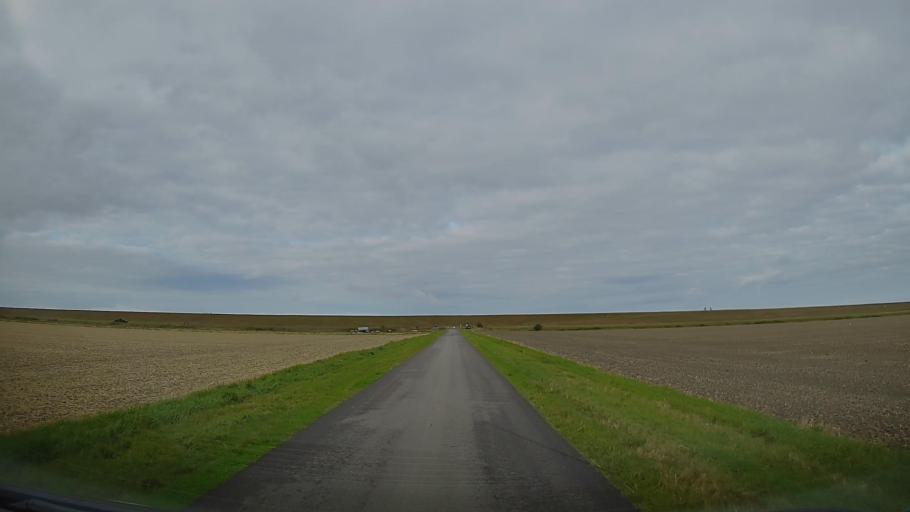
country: DE
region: Schleswig-Holstein
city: Friedrich-Wilhelm-Lubke-Koog
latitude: 54.8699
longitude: 8.6174
